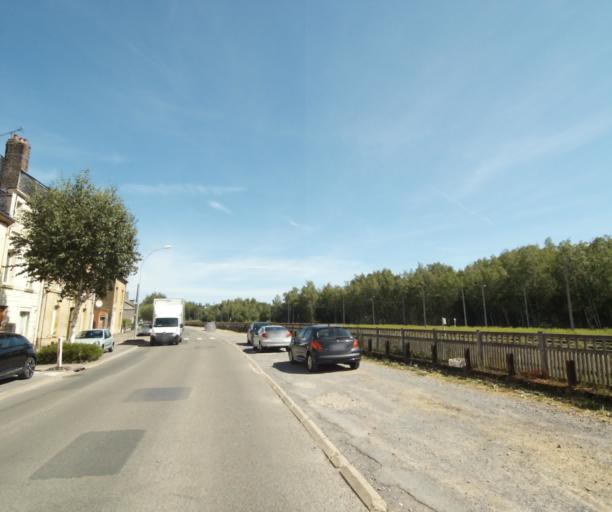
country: FR
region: Champagne-Ardenne
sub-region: Departement des Ardennes
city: Villers-Semeuse
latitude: 49.7473
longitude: 4.7363
